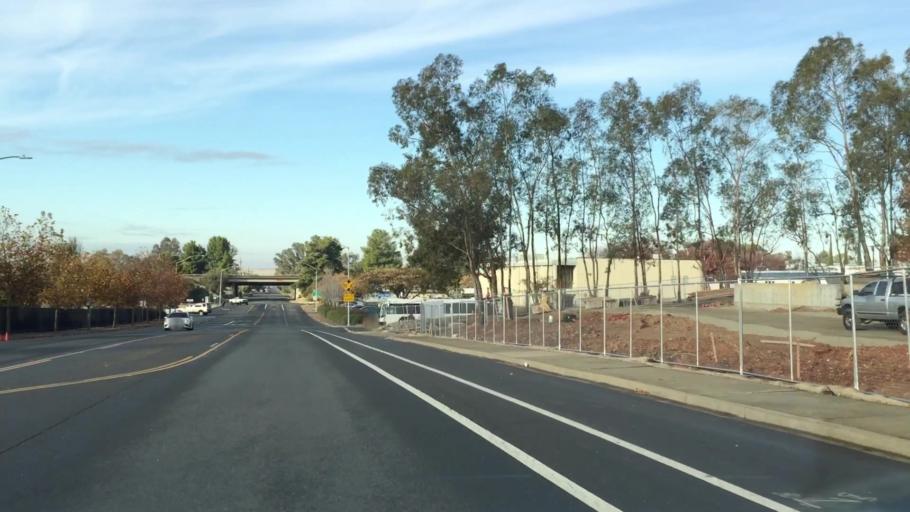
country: US
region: California
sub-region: Butte County
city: Oroville
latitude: 39.5241
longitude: -121.5698
